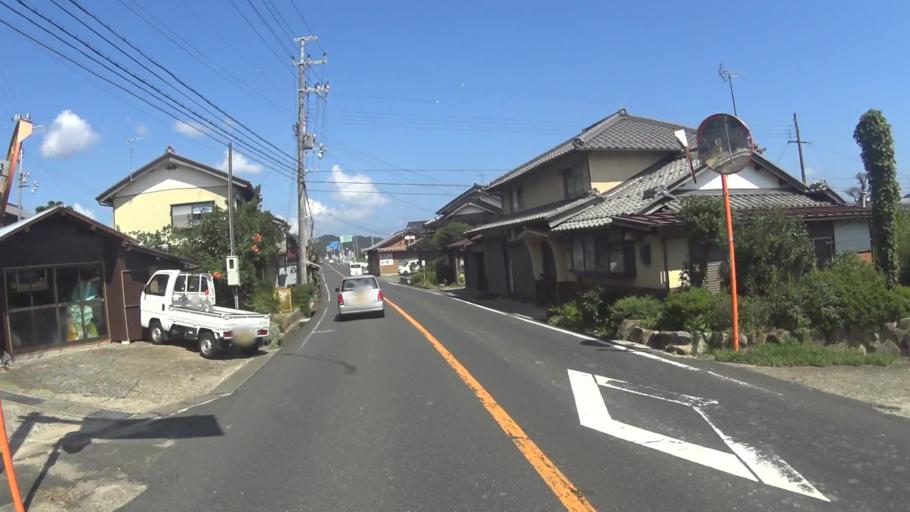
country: JP
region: Kyoto
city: Miyazu
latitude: 35.6021
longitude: 135.2194
